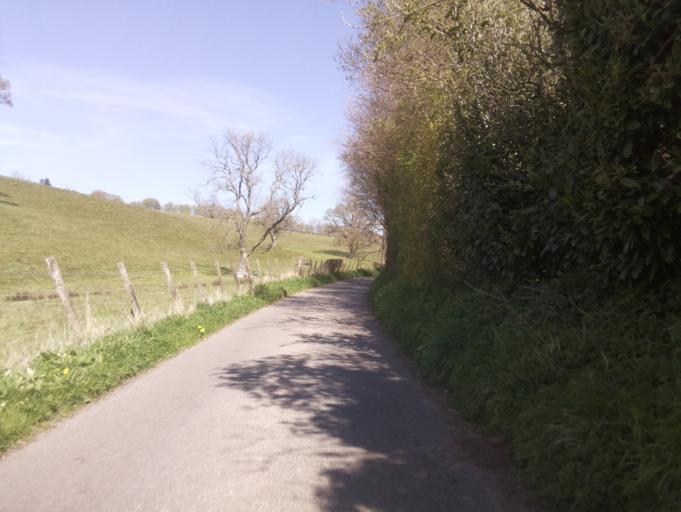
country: GB
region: Wales
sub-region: Monmouthshire
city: Caldicot
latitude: 51.6474
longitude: -2.7417
